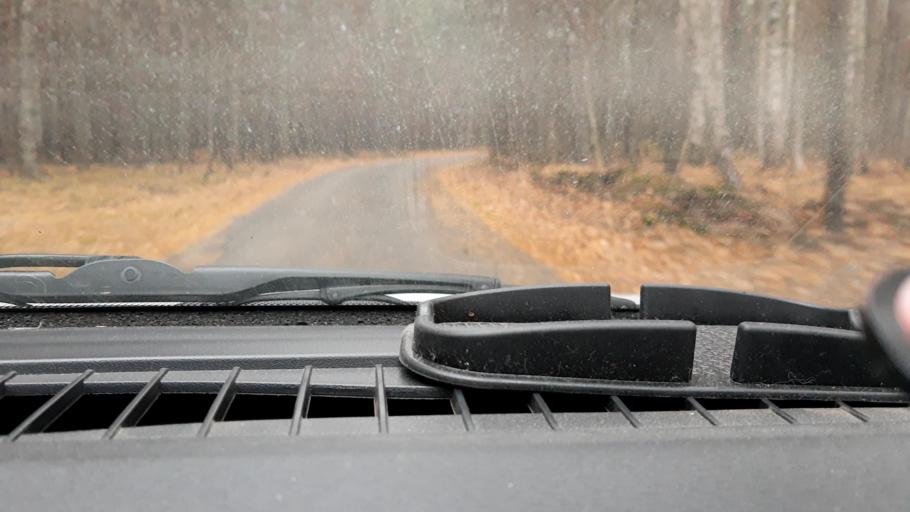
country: RU
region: Nizjnij Novgorod
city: Sitniki
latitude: 56.4239
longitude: 44.0526
